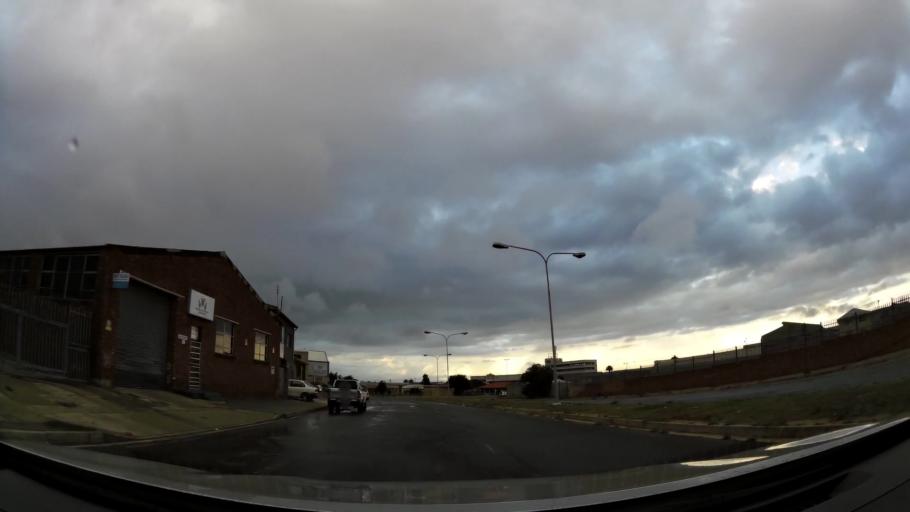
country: ZA
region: Eastern Cape
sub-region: Nelson Mandela Bay Metropolitan Municipality
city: Port Elizabeth
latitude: -33.9189
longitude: 25.5956
